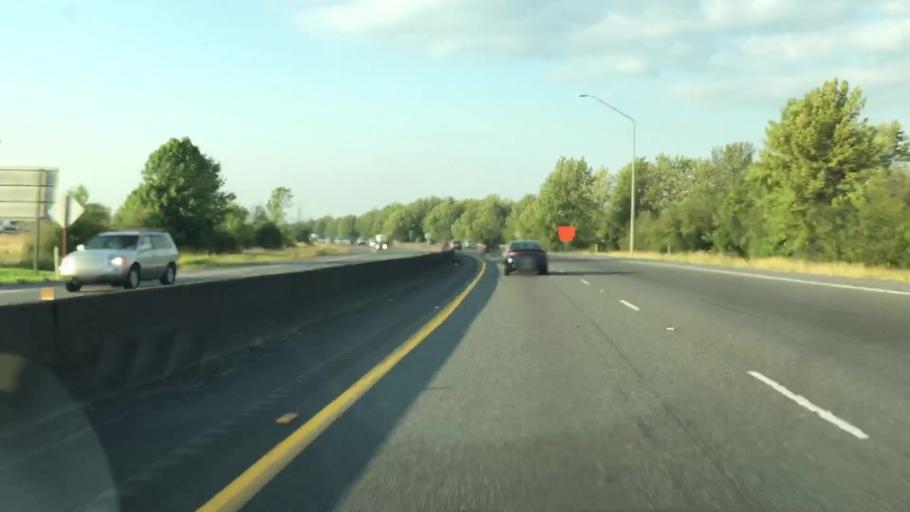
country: US
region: Washington
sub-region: Lewis County
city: Chehalis
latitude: 46.6794
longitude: -122.9721
